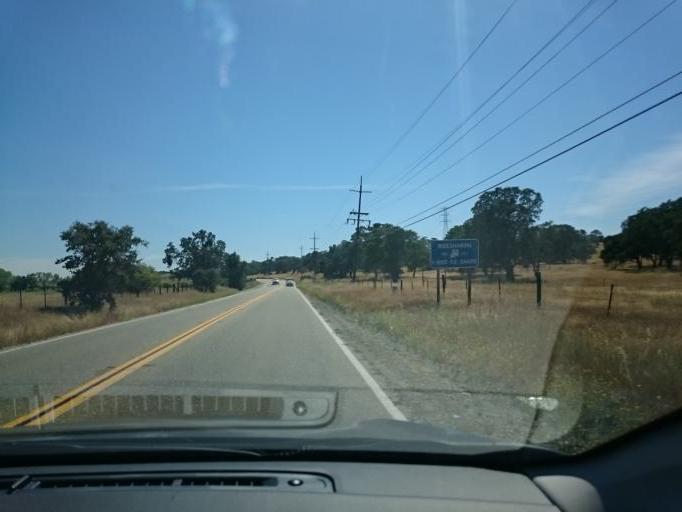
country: US
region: California
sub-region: Calaveras County
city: Valley Springs
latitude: 38.1817
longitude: -120.8281
